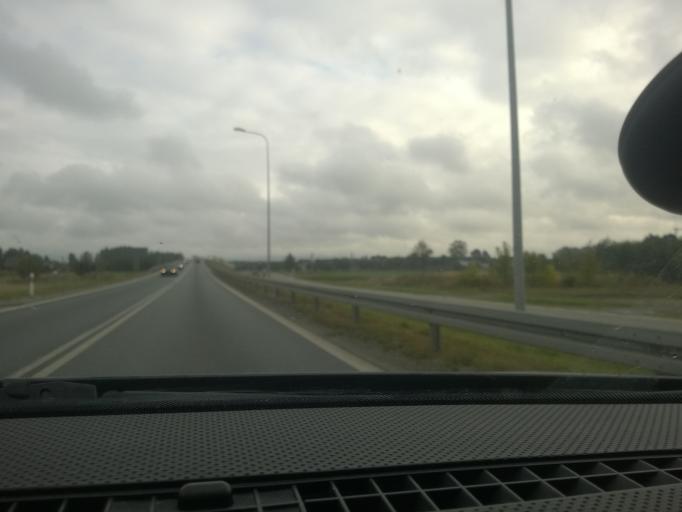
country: PL
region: Lodz Voivodeship
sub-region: Powiat sieradzki
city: Sieradz
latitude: 51.5683
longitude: 18.7025
